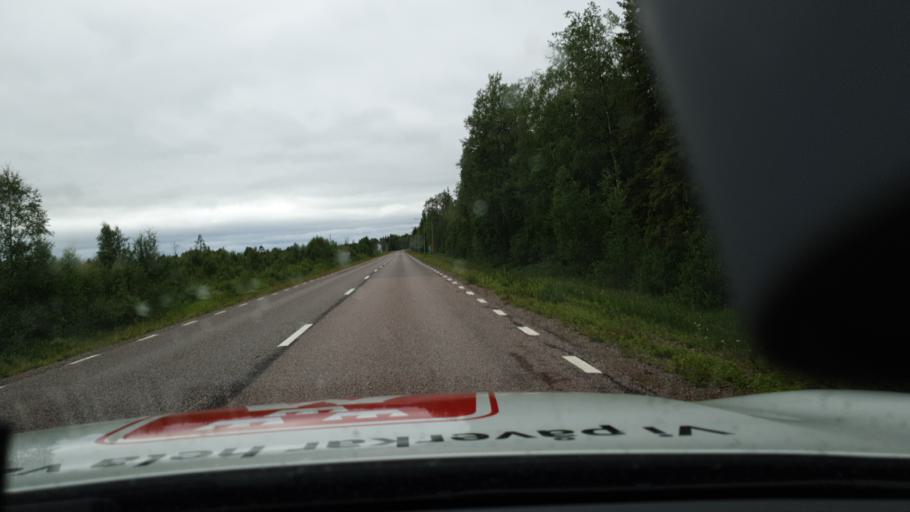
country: SE
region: Norrbotten
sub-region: Pajala Kommun
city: Pajala
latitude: 67.1991
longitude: 23.4258
